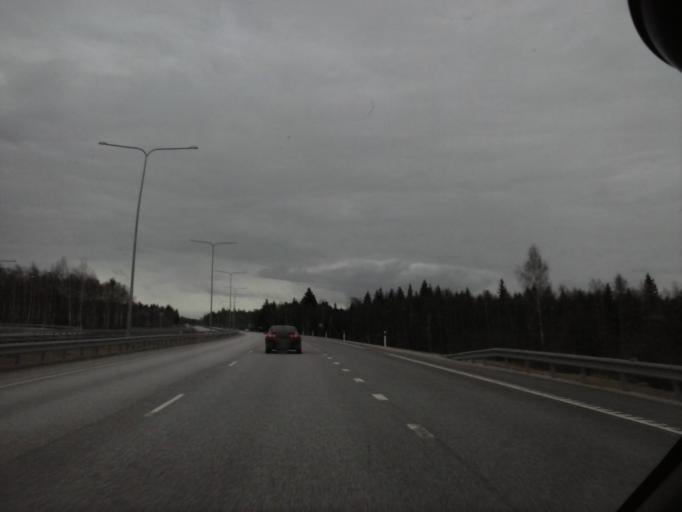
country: EE
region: Jaervamaa
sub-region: Paide linn
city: Paide
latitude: 58.9001
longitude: 25.6413
